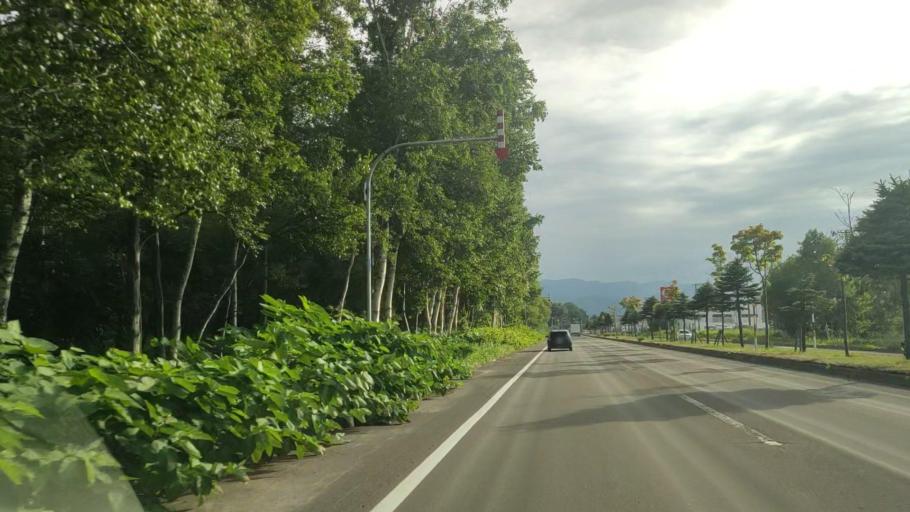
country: JP
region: Hokkaido
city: Ishikari
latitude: 43.1632
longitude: 141.2856
